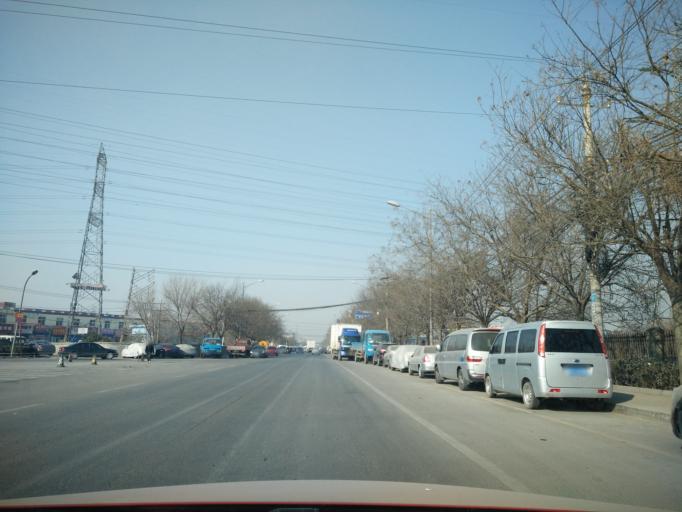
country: CN
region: Beijing
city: Jiugong
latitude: 39.8300
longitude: 116.4965
